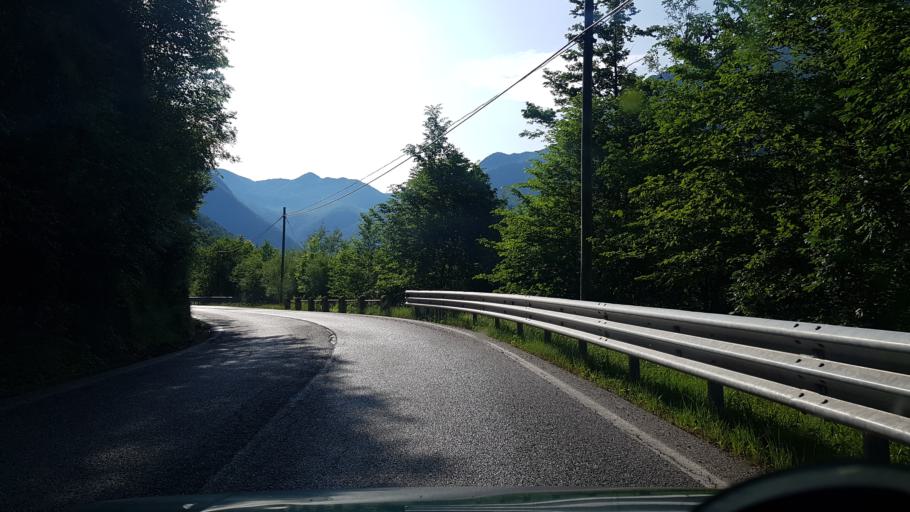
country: IT
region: Friuli Venezia Giulia
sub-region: Provincia di Udine
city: Lusevera
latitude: 46.3043
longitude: 13.2961
